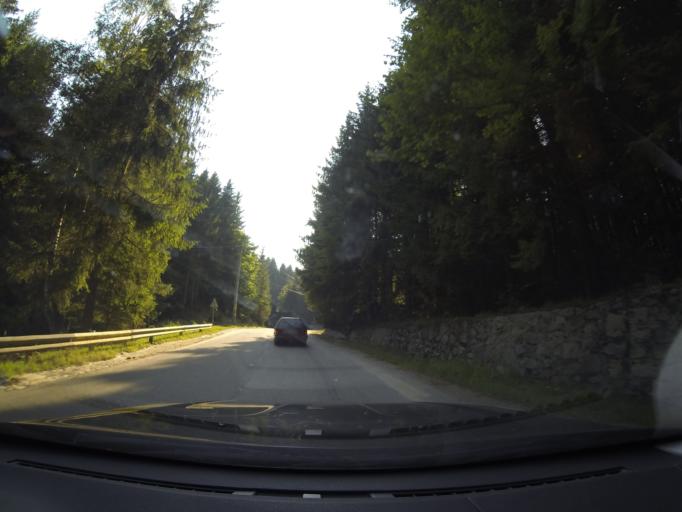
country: RO
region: Arges
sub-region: Comuna Arefu
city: Arefu
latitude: 45.4072
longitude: 24.6379
